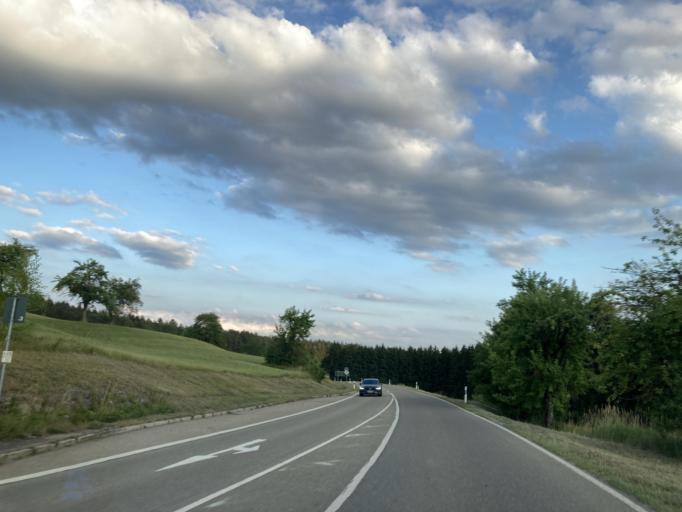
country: DE
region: Baden-Wuerttemberg
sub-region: Karlsruhe Region
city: Dornstetten
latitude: 48.4585
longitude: 8.5052
